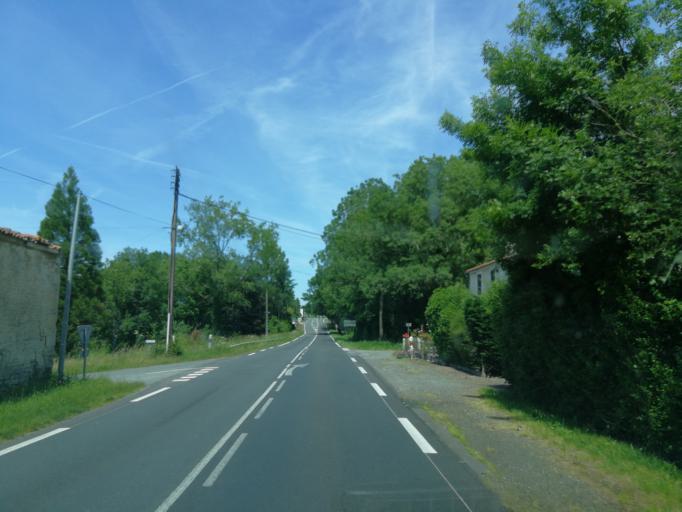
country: FR
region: Pays de la Loire
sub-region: Departement de la Vendee
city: Pissotte
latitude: 46.5234
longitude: -0.8078
